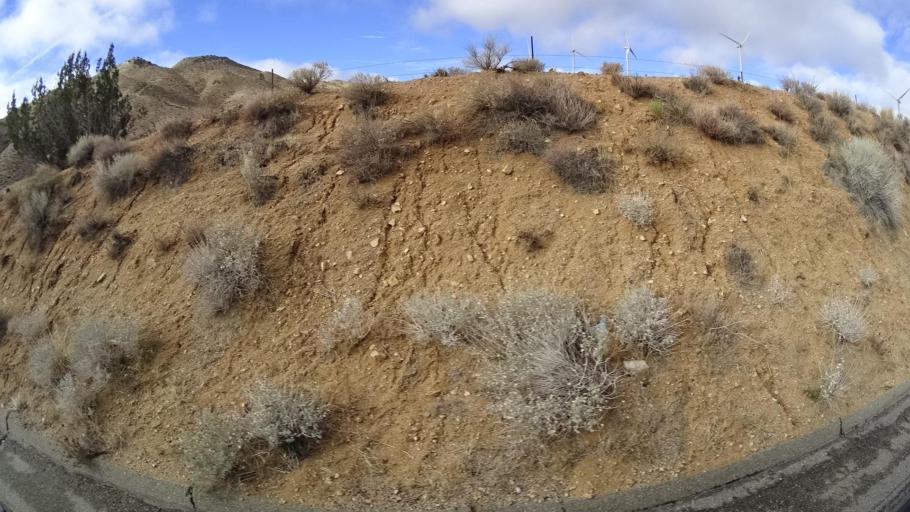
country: US
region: California
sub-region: Kern County
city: Tehachapi
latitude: 35.0213
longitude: -118.3501
